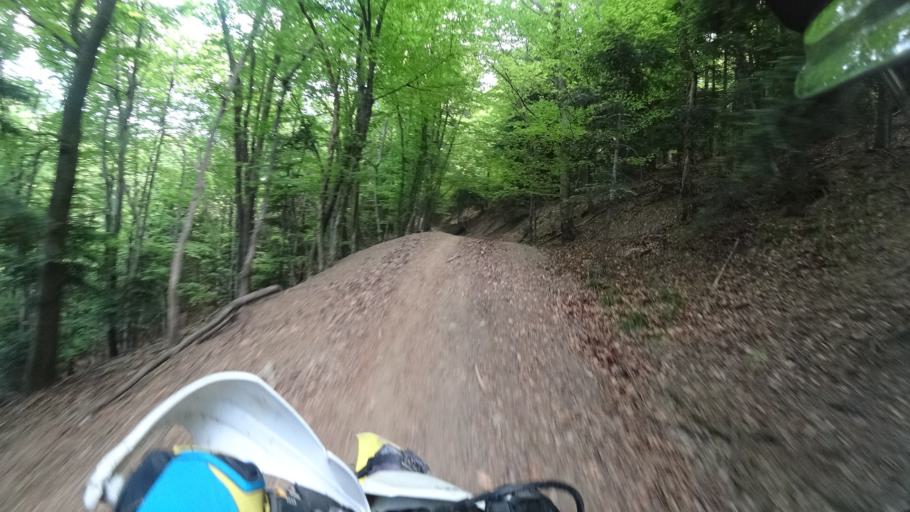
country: HR
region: Grad Zagreb
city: Kasina
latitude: 45.9247
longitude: 15.9510
